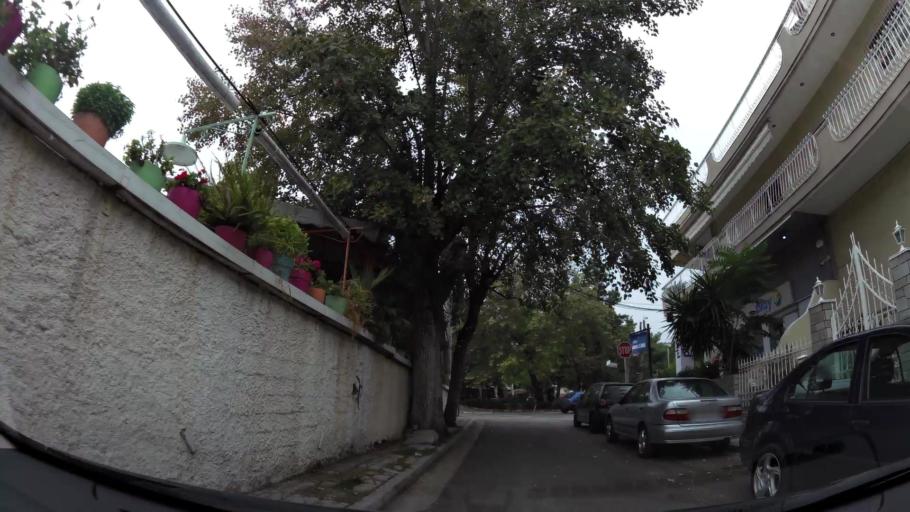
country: GR
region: Attica
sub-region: Nomarchia Athinas
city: Chaidari
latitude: 38.0023
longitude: 23.6638
